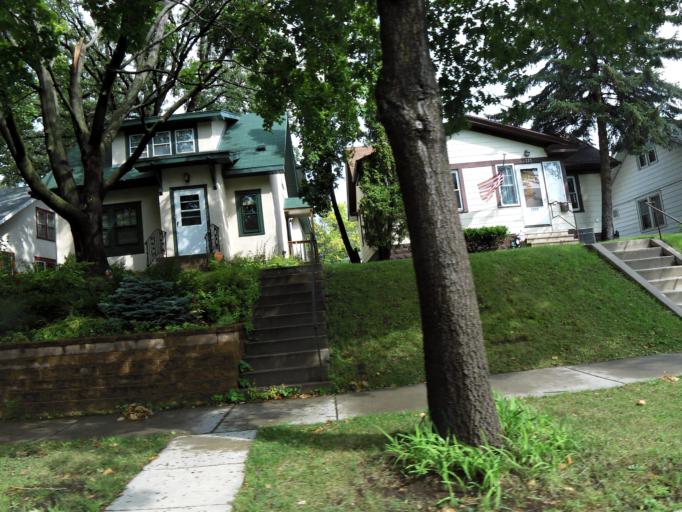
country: US
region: Minnesota
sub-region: Dakota County
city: Mendota Heights
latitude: 44.9307
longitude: -93.1732
